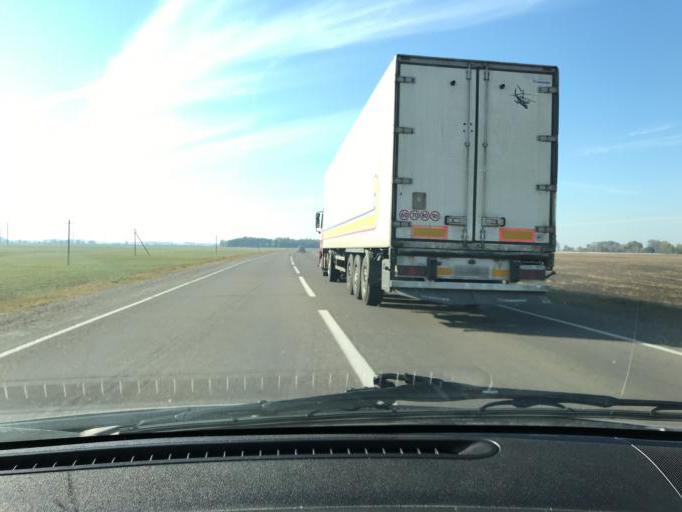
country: BY
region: Brest
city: Asnyezhytsy
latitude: 52.2776
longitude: 26.3977
